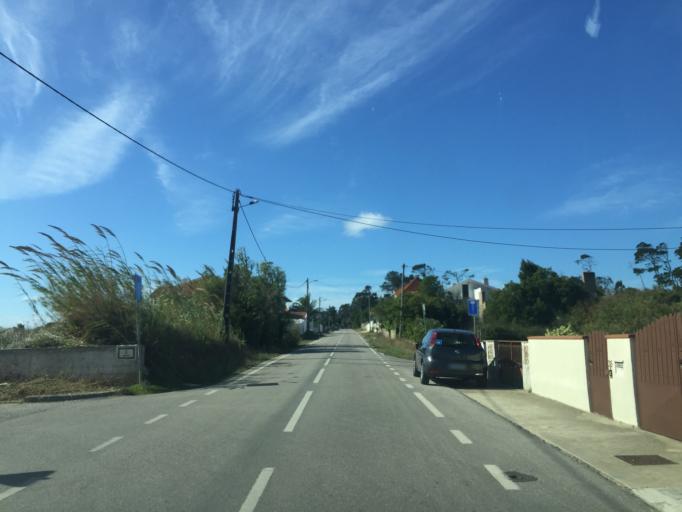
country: PT
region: Coimbra
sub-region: Figueira da Foz
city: Buarcos
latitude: 40.1915
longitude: -8.8689
